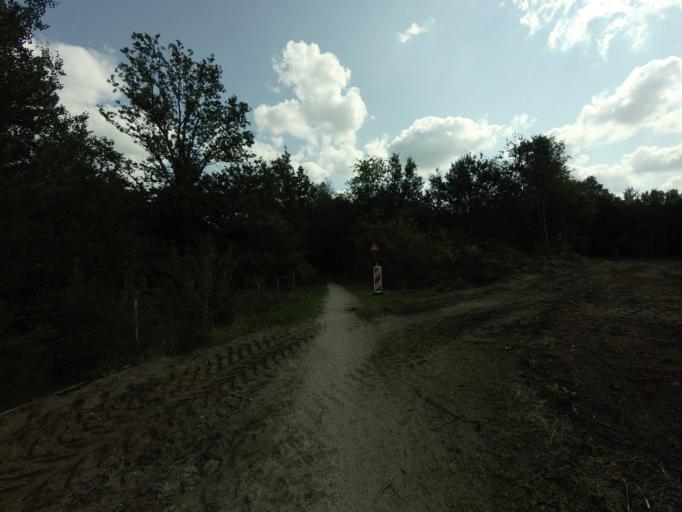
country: NL
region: Drenthe
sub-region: Gemeente Westerveld
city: Dwingeloo
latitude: 52.8820
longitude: 6.4012
